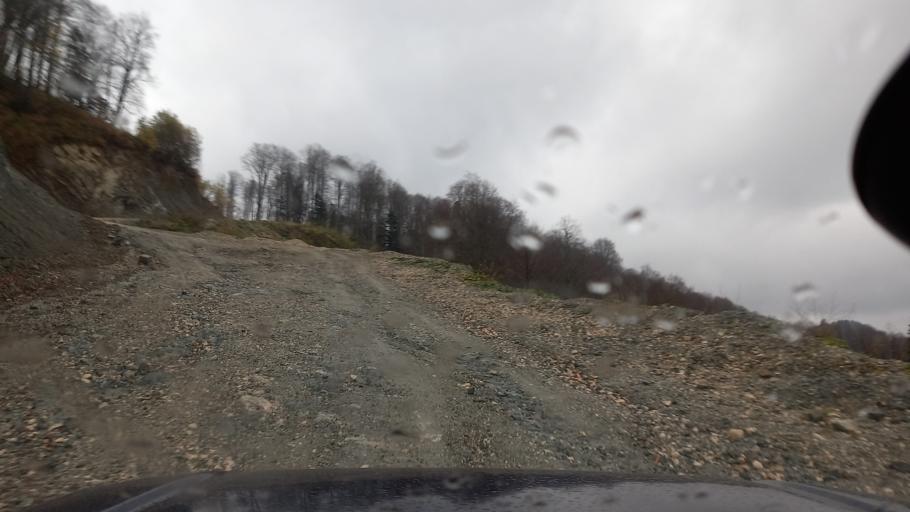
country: RU
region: Krasnodarskiy
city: Dagomys
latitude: 43.9873
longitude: 39.8506
